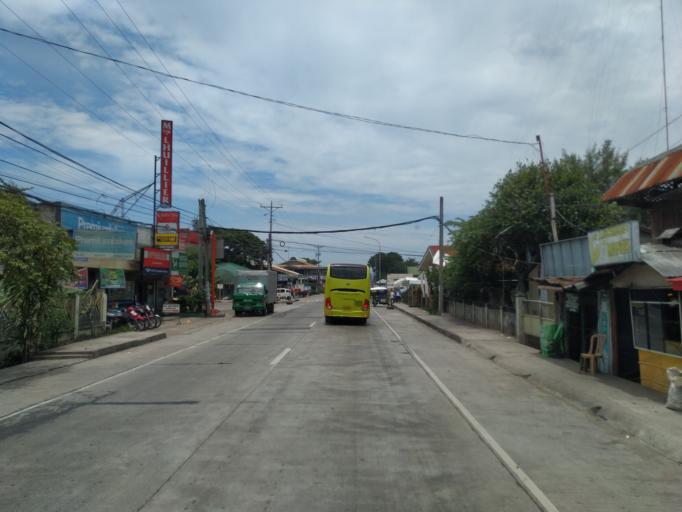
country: PH
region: Central Visayas
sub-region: Province of Negros Oriental
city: Sibulan
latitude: 9.3578
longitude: 123.2849
